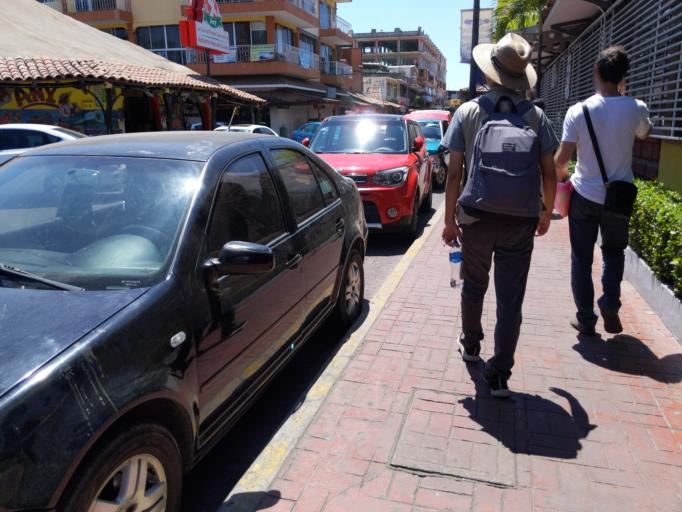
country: MX
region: Guerrero
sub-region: Zihuatanejo de Azueta
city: Ixtapa-Zihuatanejo
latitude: 17.6409
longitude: -101.5573
